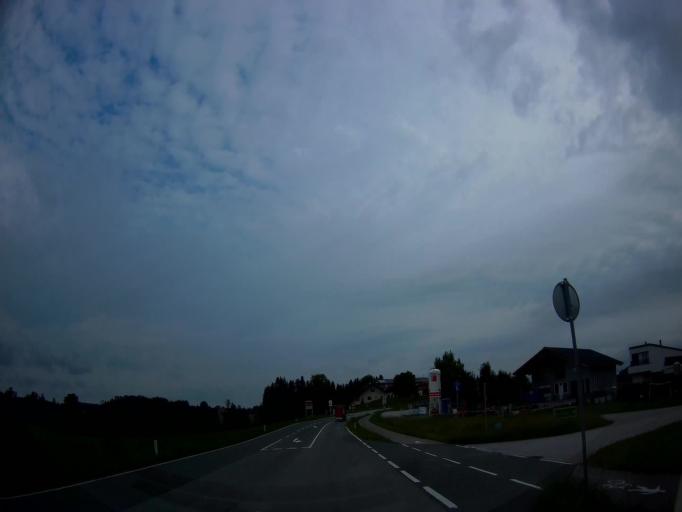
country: AT
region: Salzburg
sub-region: Politischer Bezirk Salzburg-Umgebung
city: Mattsee
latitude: 47.9942
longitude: 13.1175
